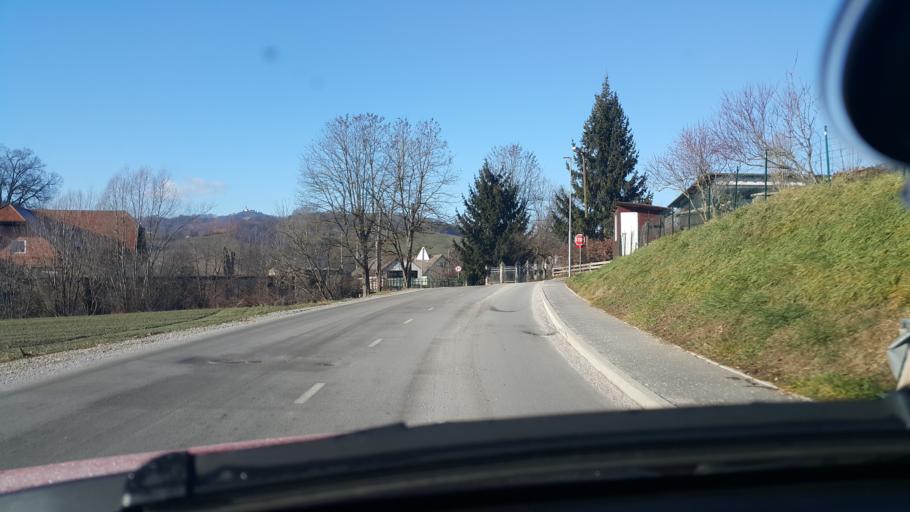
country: SI
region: Pesnica
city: Pesnica pri Mariboru
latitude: 46.6050
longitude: 15.6502
